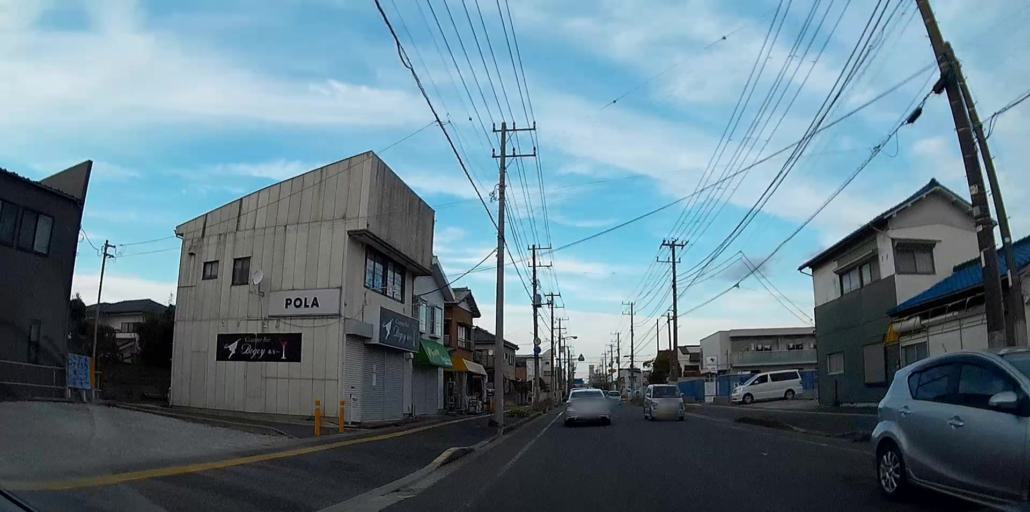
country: JP
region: Chiba
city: Ichihara
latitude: 35.4730
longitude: 140.0432
